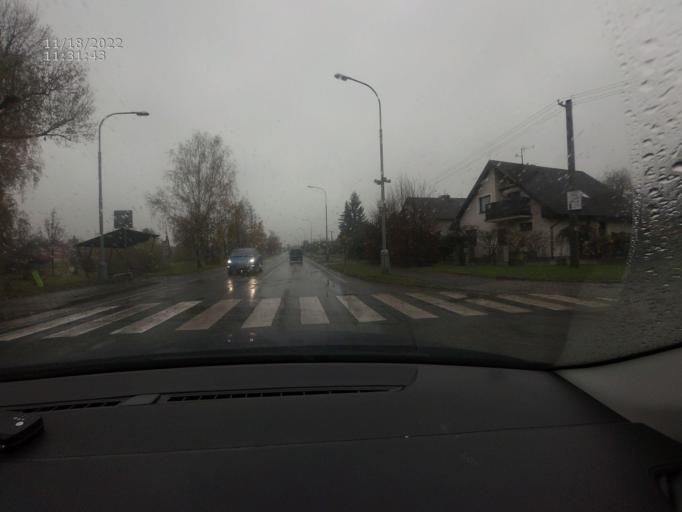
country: CZ
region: Plzensky
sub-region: Okres Rokycany
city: Rokycany
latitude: 49.7373
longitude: 13.5845
